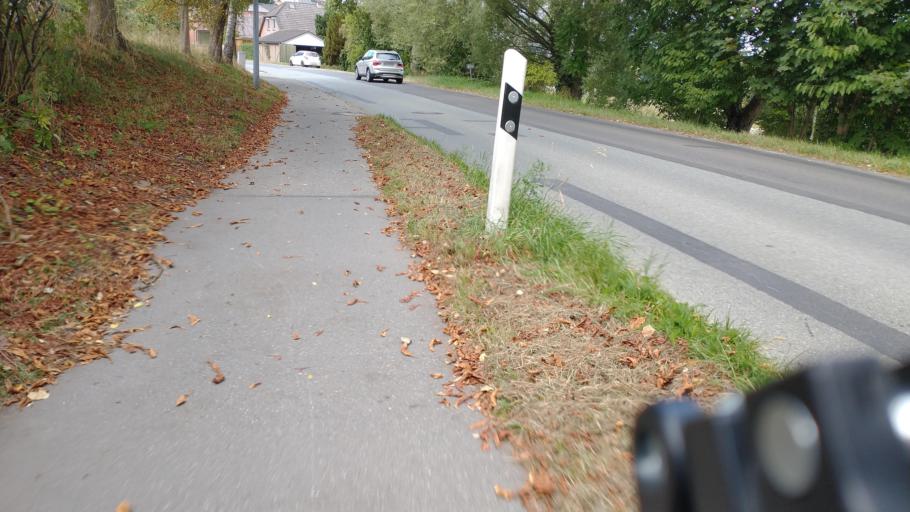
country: DE
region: Schleswig-Holstein
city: Rumpel
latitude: 53.8124
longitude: 10.3432
